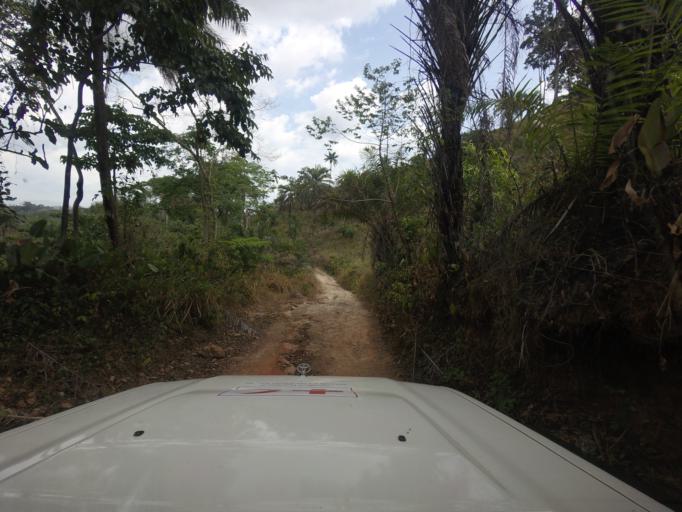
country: LR
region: Lofa
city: Voinjama
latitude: 8.3933
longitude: -9.6271
